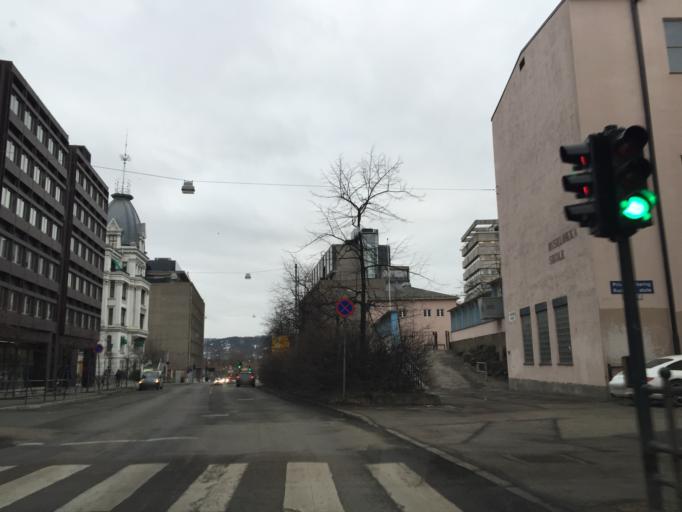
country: NO
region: Oslo
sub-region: Oslo
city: Oslo
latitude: 59.9139
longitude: 10.7253
